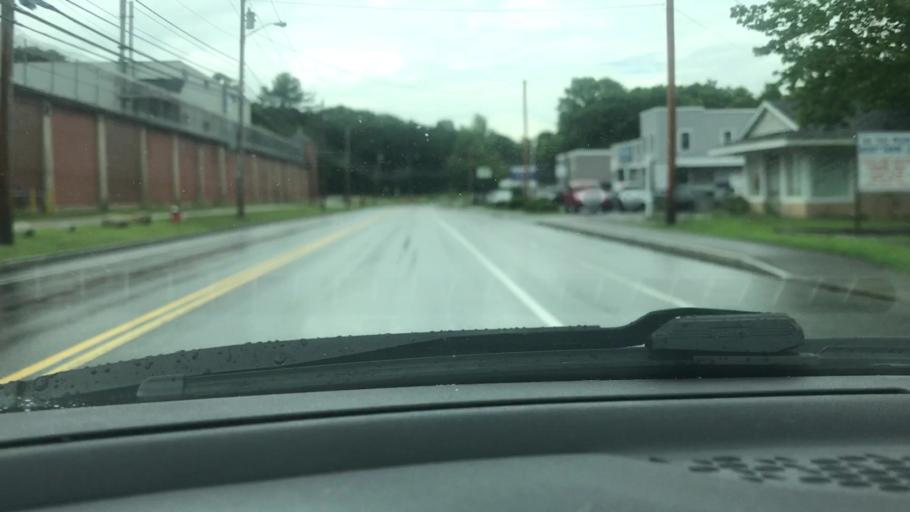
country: US
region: New Hampshire
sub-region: Merrimack County
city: East Concord
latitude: 43.2279
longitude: -71.5573
